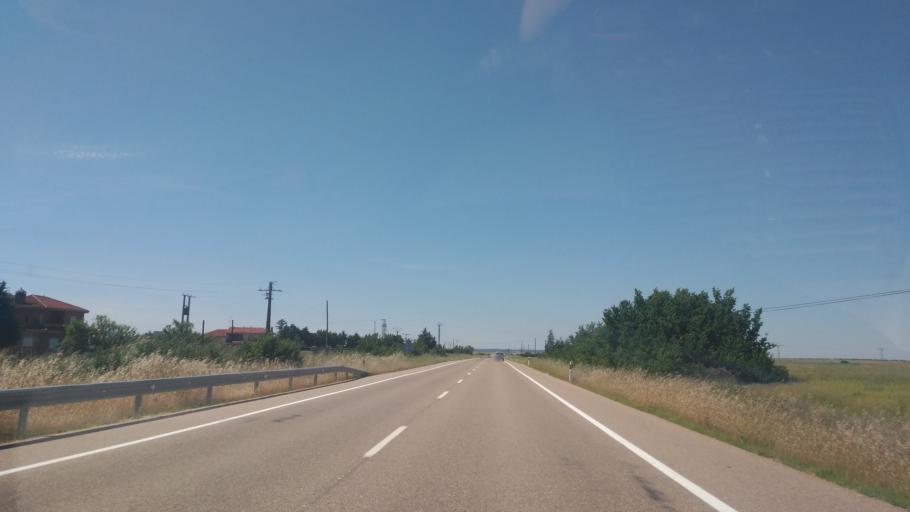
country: ES
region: Castille and Leon
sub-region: Provincia de Salamanca
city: Castellanos de Villiquera
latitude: 41.0610
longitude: -5.6851
